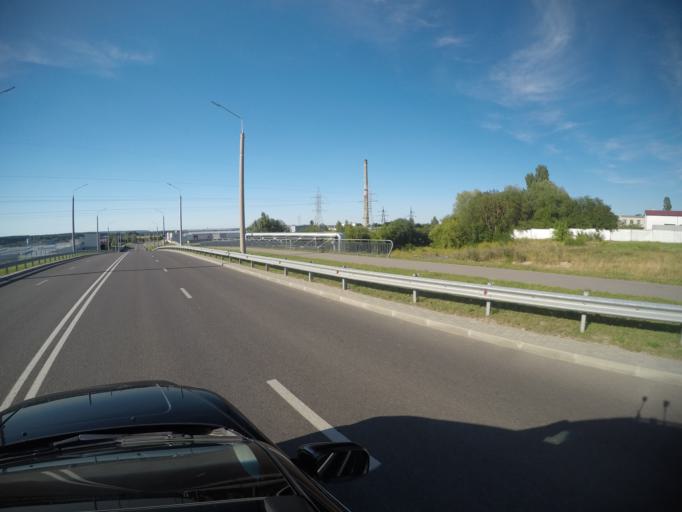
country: BY
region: Grodnenskaya
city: Hrodna
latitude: 53.7166
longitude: 23.8245
